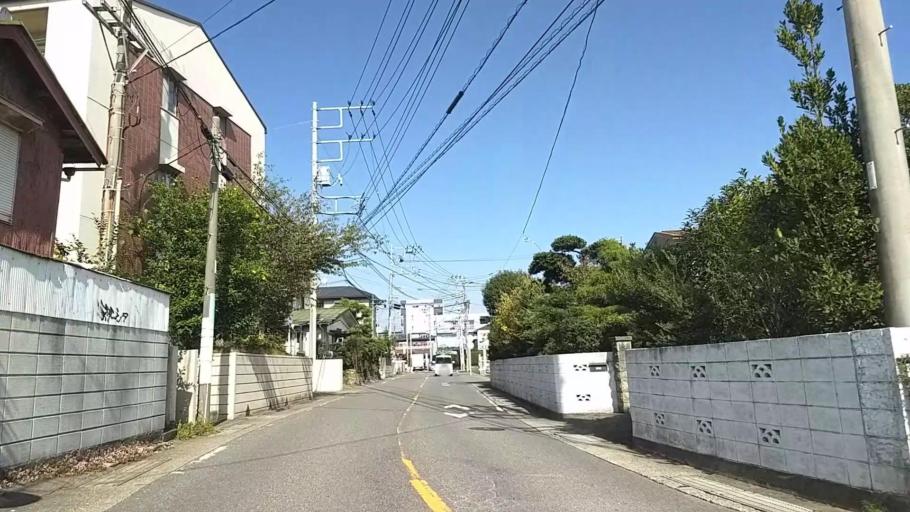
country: JP
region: Kanagawa
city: Atsugi
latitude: 35.4453
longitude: 139.3545
